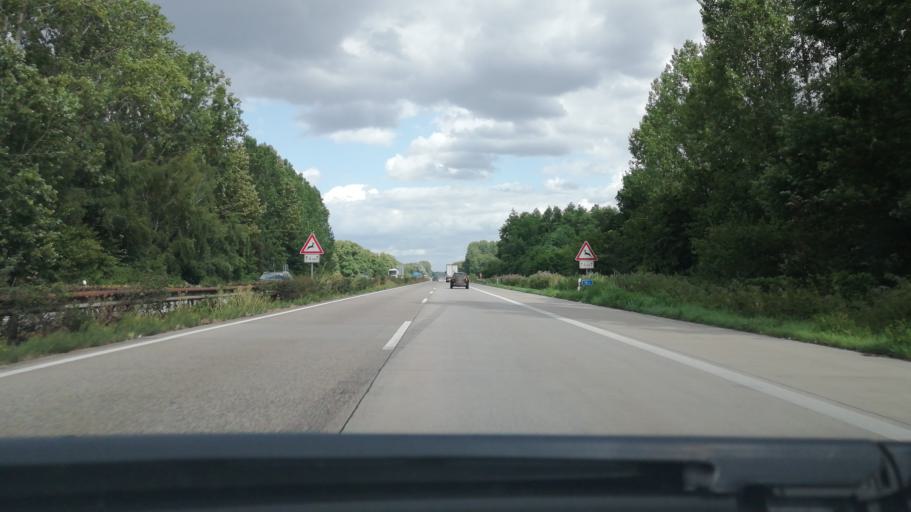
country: DE
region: North Rhine-Westphalia
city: Kempen
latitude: 51.4089
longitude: 6.4270
